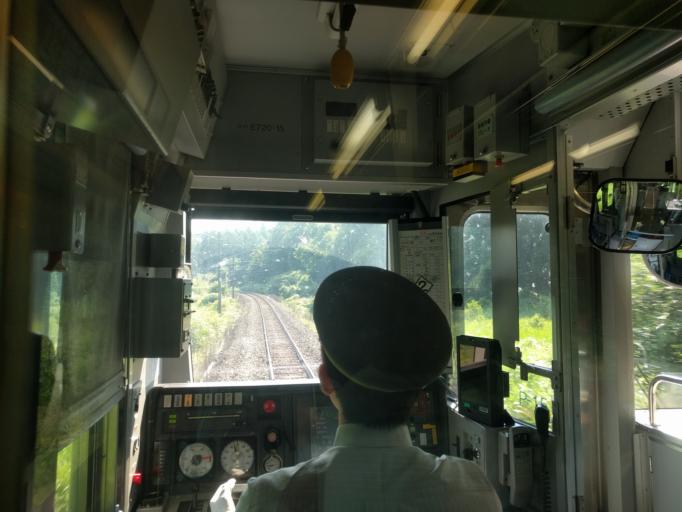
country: JP
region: Fukushima
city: Inawashiro
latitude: 37.5431
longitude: 140.0250
